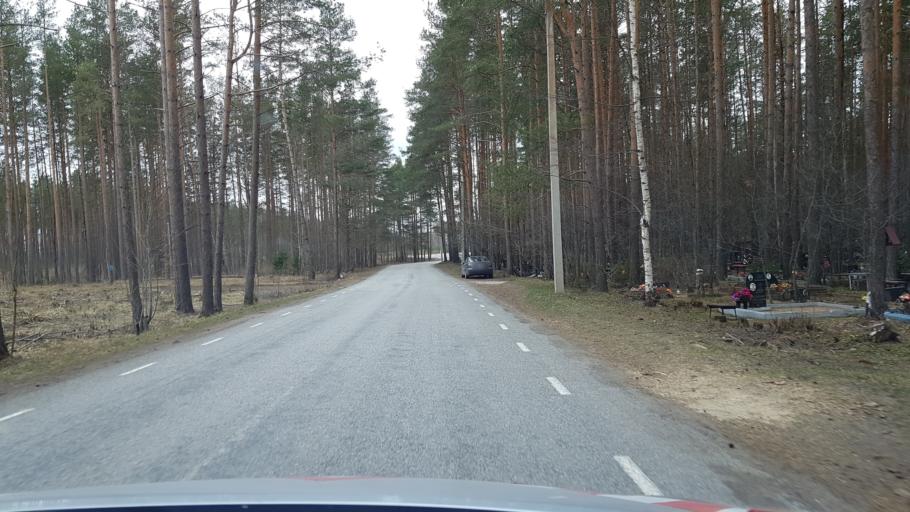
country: EE
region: Ida-Virumaa
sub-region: Narva-Joesuu linn
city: Narva-Joesuu
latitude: 59.4211
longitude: 28.1101
